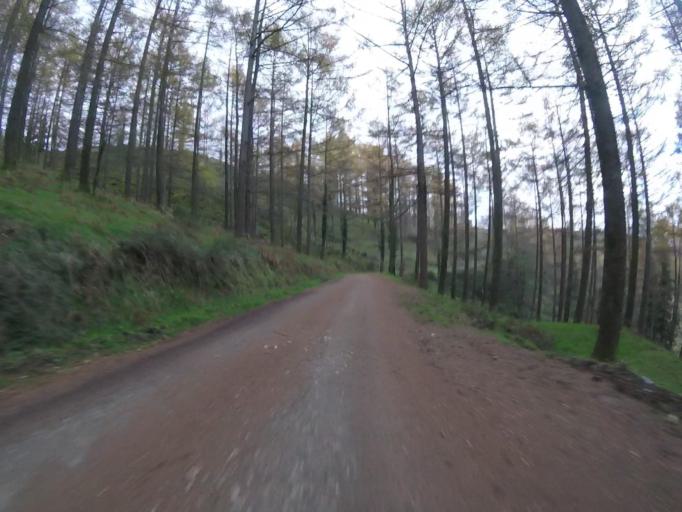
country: ES
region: Navarre
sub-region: Provincia de Navarra
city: Goizueta
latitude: 43.1821
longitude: -1.8133
